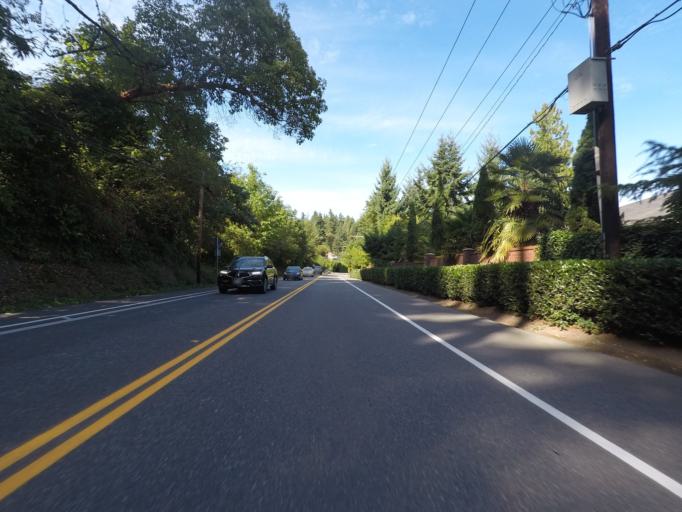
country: US
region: Washington
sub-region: King County
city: Inglewood-Finn Hill
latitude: 47.7000
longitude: -122.2285
